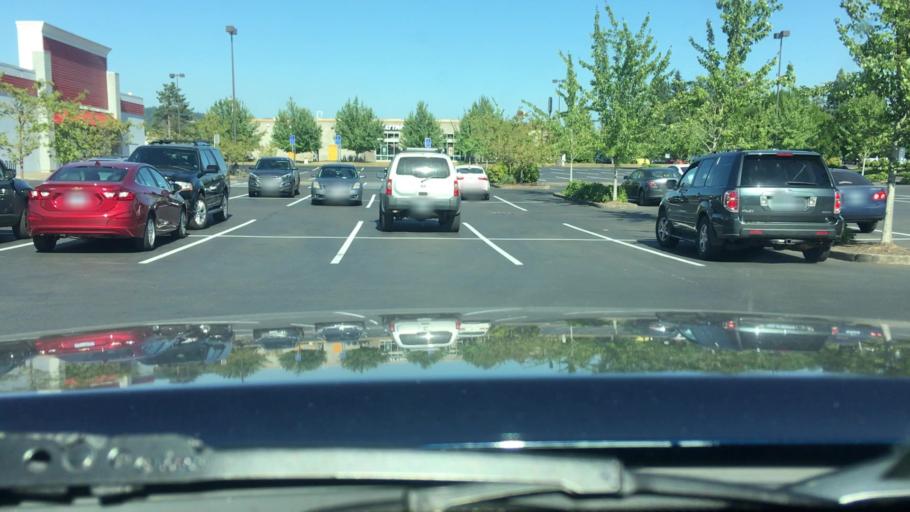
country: US
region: Oregon
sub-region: Lane County
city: Springfield
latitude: 44.0821
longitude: -123.0449
